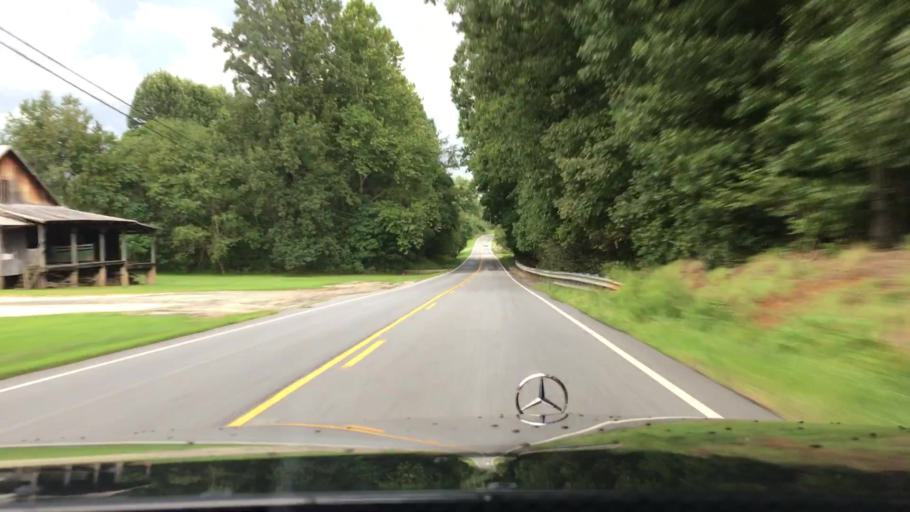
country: US
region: Virginia
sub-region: Nelson County
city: Lovingston
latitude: 37.7925
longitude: -78.9744
